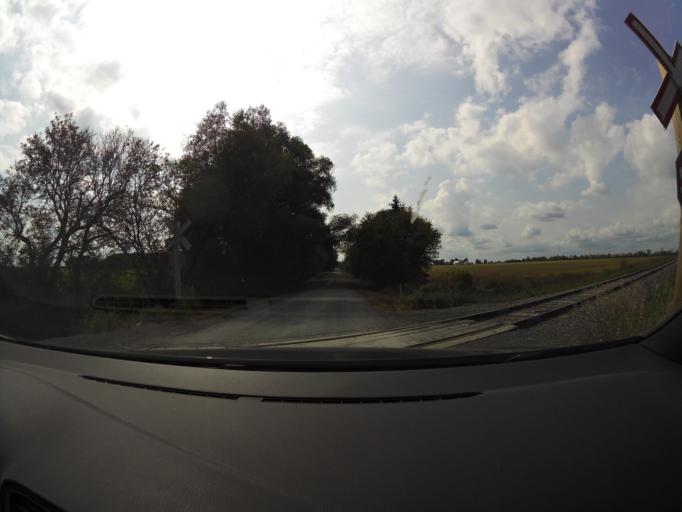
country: CA
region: Ontario
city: Arnprior
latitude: 45.3771
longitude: -76.1527
